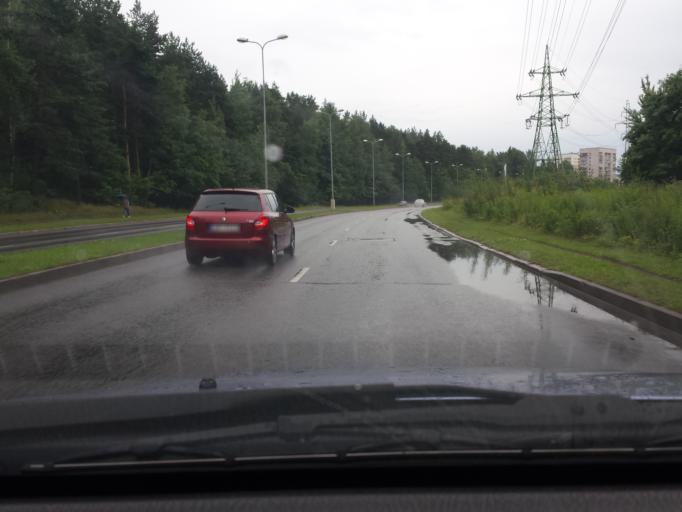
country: LV
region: Riga
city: Jaunciems
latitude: 56.9650
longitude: 24.1990
